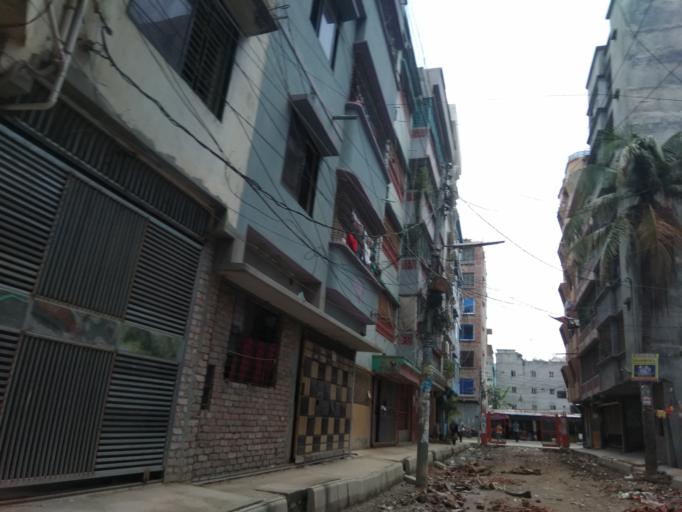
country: BD
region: Dhaka
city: Tungi
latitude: 23.8287
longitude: 90.3674
